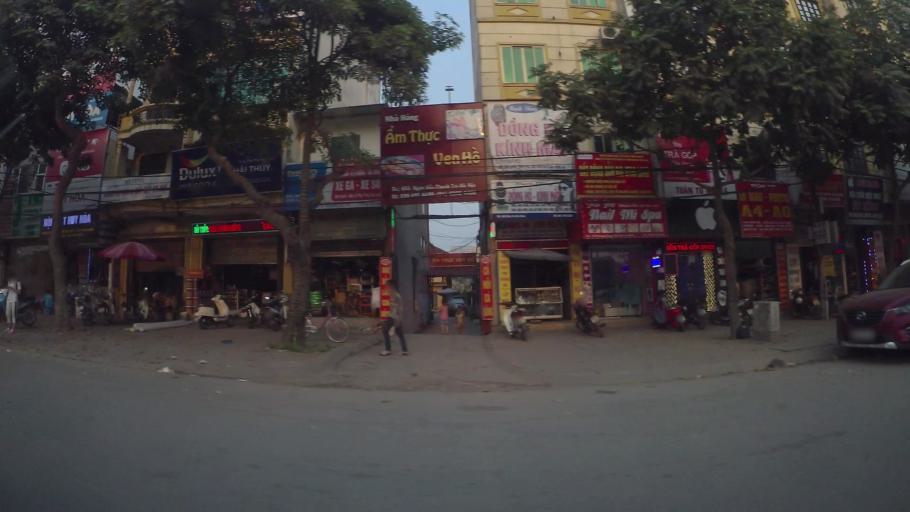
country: VN
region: Ha Noi
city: Van Dien
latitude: 20.9441
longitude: 105.8444
